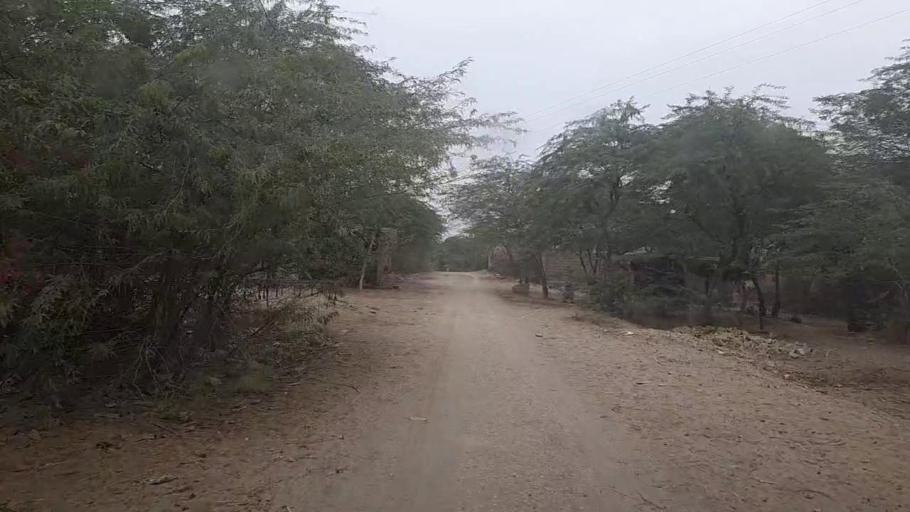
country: PK
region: Sindh
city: Gambat
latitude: 27.3492
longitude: 68.6013
